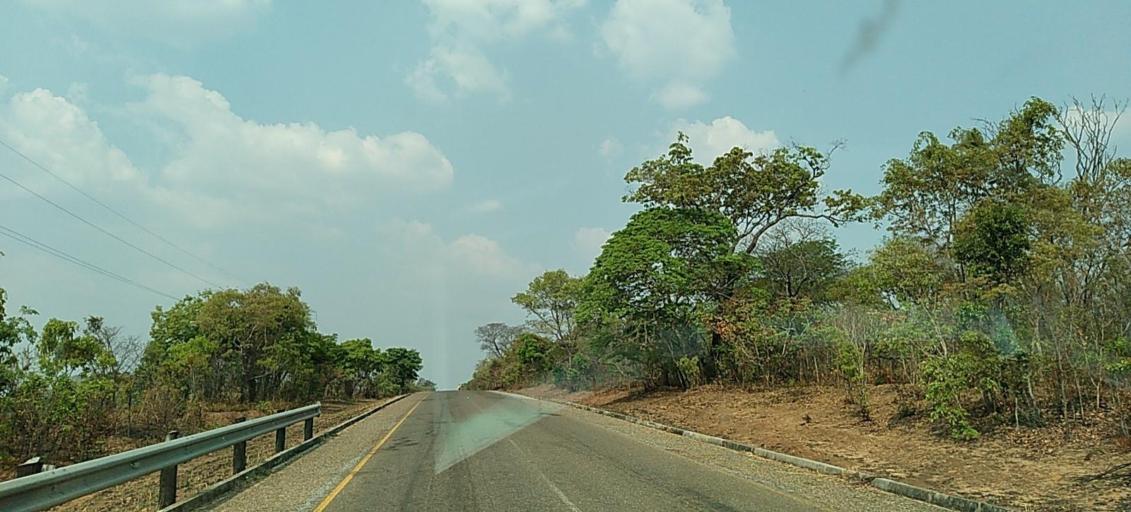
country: ZM
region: North-Western
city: Kabompo
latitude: -13.6094
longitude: 24.1530
